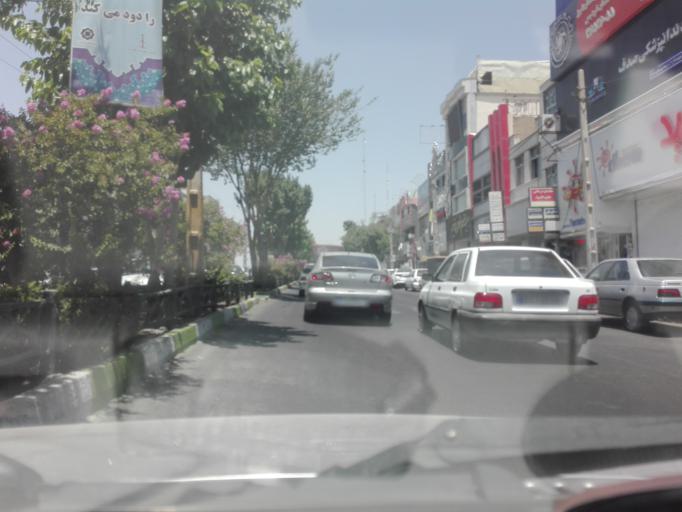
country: IR
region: Tehran
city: Shahre Jadide Andisheh
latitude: 35.7211
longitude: 50.9875
